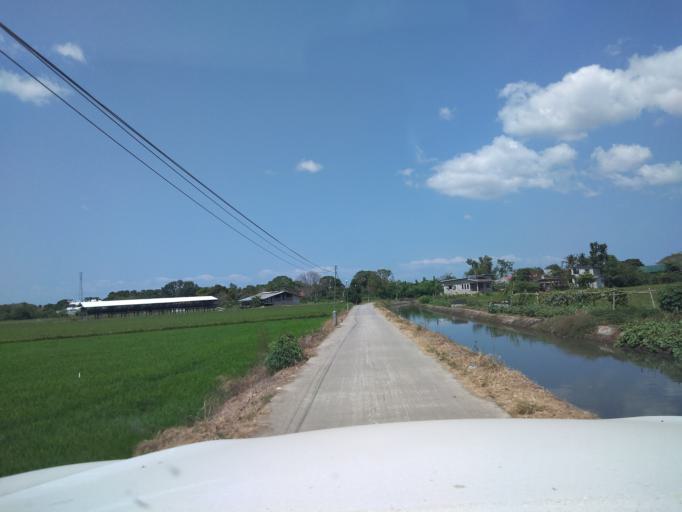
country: PH
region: Central Luzon
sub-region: Province of Pampanga
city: Bahay Pare
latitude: 15.0475
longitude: 120.8749
